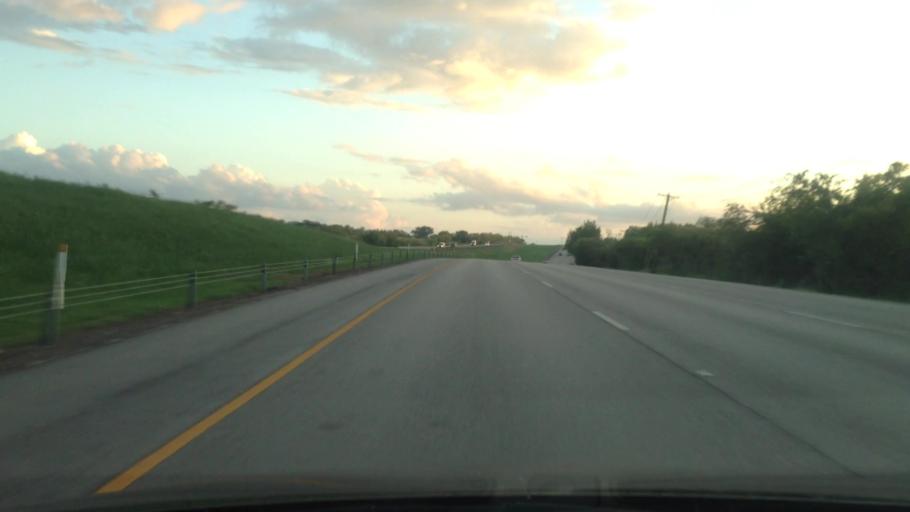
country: US
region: Texas
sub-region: Tarrant County
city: Benbrook
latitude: 32.6555
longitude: -97.4953
